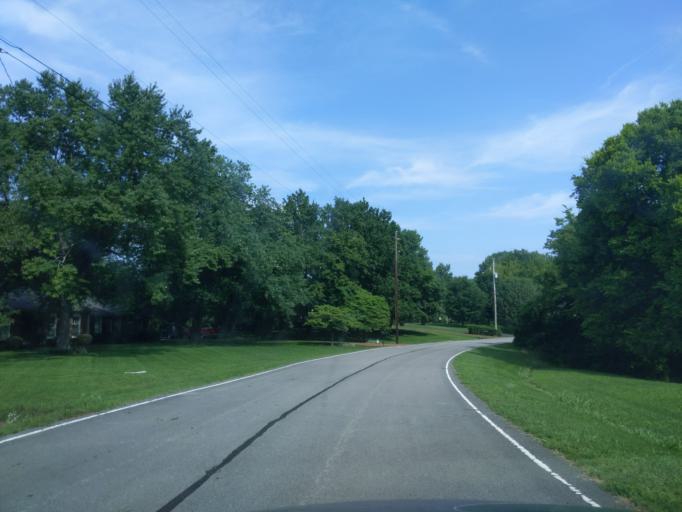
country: US
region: Tennessee
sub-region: Williamson County
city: Brentwood Estates
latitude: 36.0298
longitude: -86.7411
